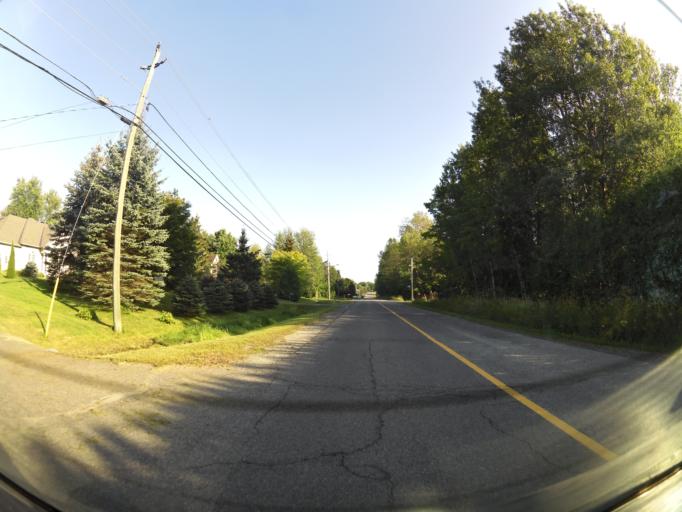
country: CA
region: Ontario
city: Clarence-Rockland
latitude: 45.5072
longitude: -75.4532
